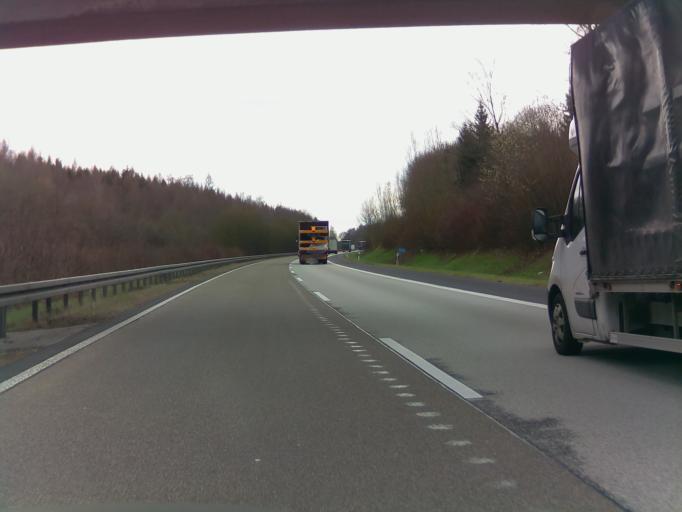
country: DE
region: Hesse
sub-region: Regierungsbezirk Darmstadt
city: Echzell
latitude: 50.3885
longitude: 8.9355
